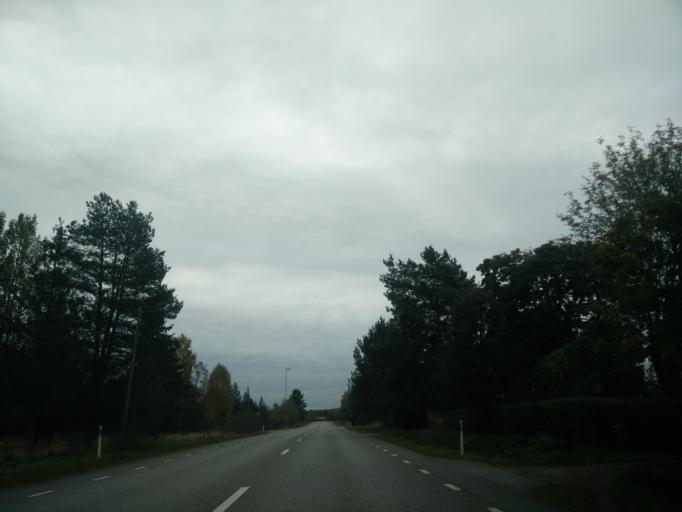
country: SE
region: Gaevleborg
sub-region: Gavle Kommun
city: Norrsundet
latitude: 60.9029
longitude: 17.0469
